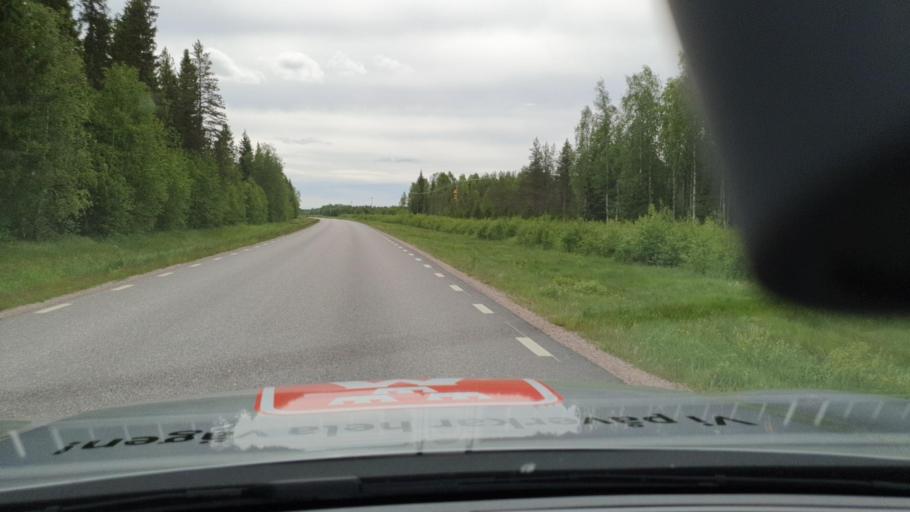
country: SE
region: Norrbotten
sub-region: Kalix Kommun
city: Kalix
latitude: 65.8950
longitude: 23.4637
